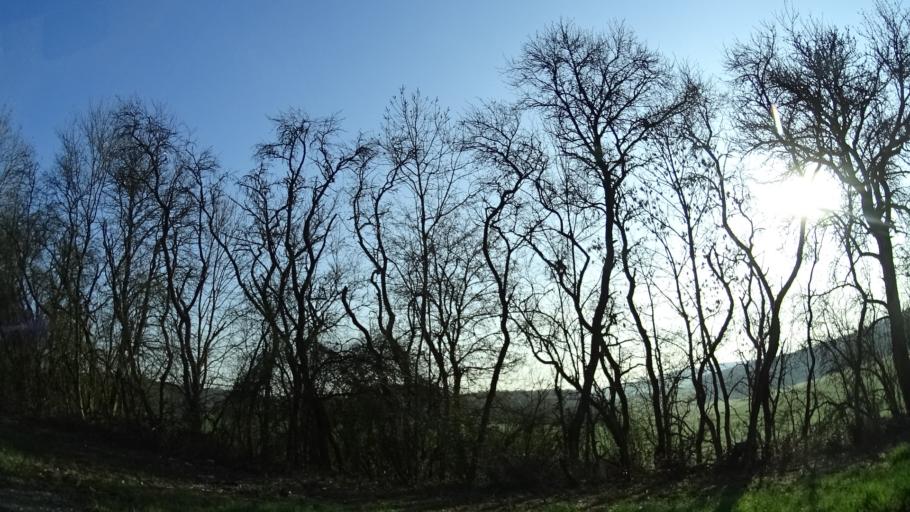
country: DE
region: Rheinland-Pfalz
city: Sien
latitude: 49.6891
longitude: 7.5157
